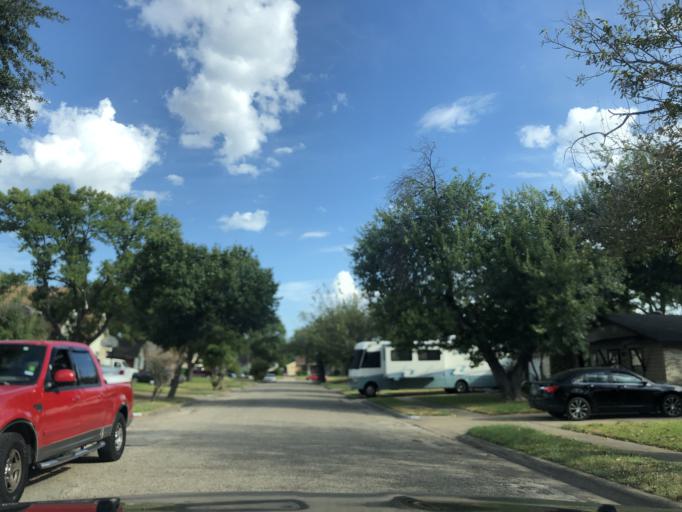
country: US
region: Texas
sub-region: Dallas County
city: Garland
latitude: 32.8855
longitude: -96.6648
